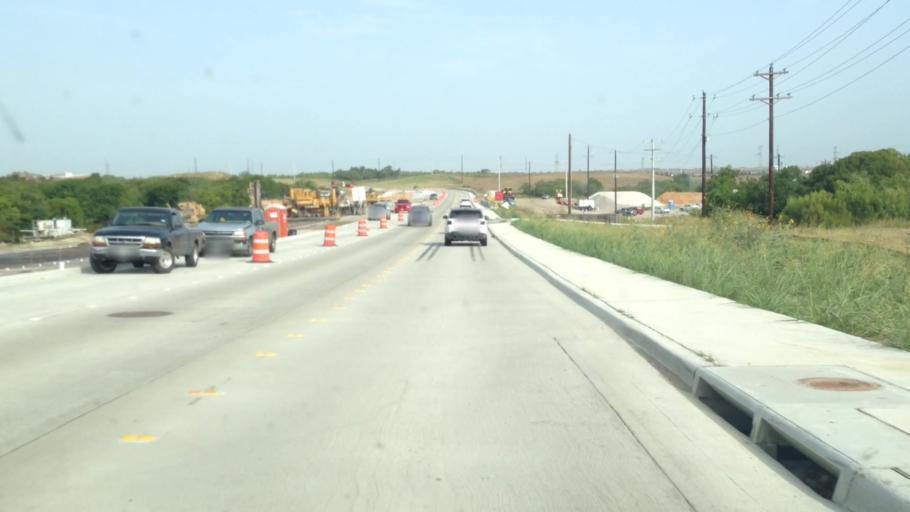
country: US
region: Texas
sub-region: Denton County
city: The Colony
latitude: 33.0453
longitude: -96.8911
